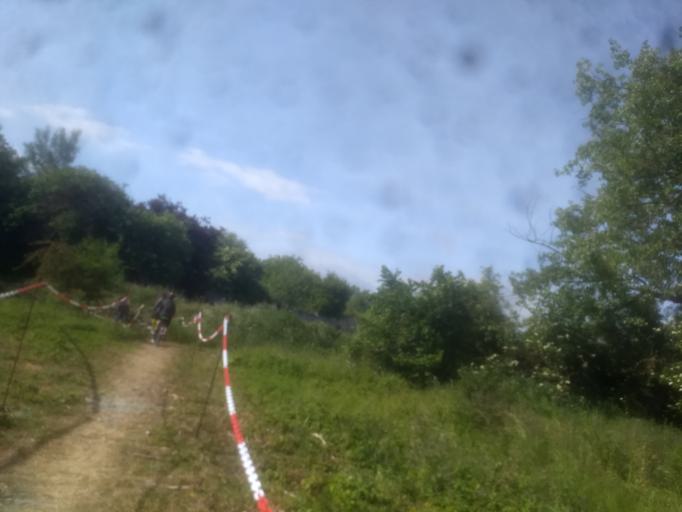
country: FR
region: Nord-Pas-de-Calais
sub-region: Departement du Pas-de-Calais
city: Feuchy
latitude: 50.3031
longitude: 2.8256
